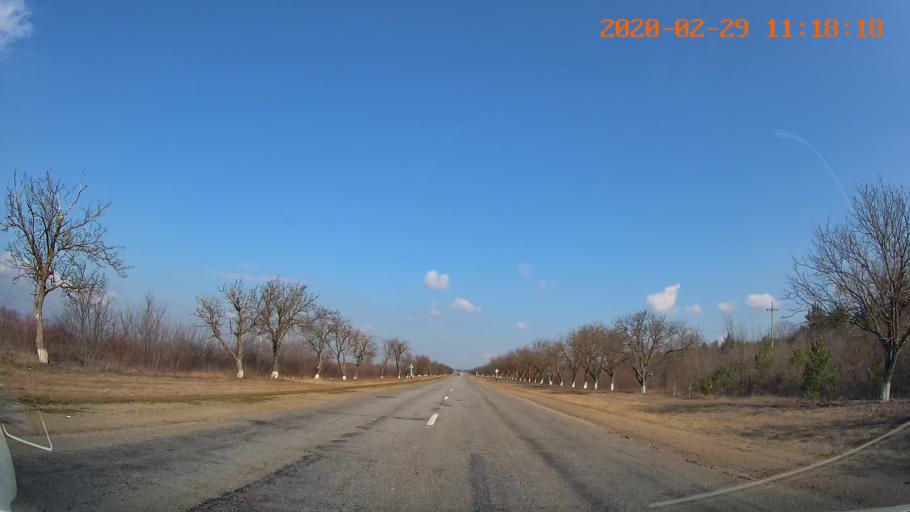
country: MD
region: Telenesti
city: Cocieri
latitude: 47.3330
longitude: 29.1726
